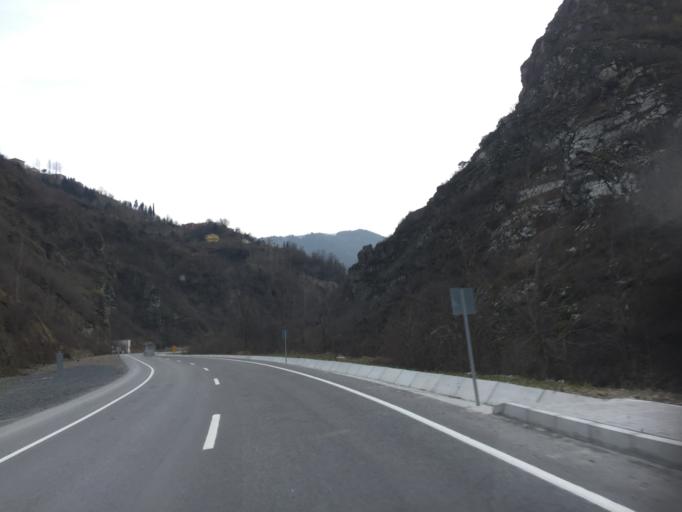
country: TR
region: Trabzon
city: Macka
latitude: 40.7702
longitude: 39.5651
